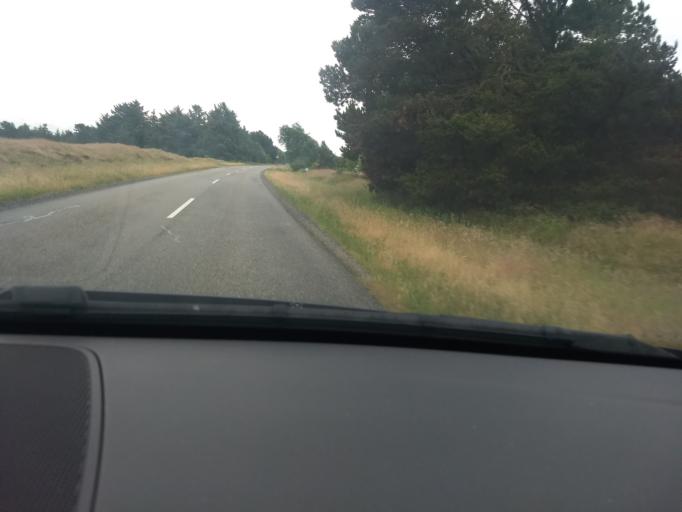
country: DK
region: South Denmark
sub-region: Fano Kommune
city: Nordby
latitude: 55.3567
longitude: 8.4639
